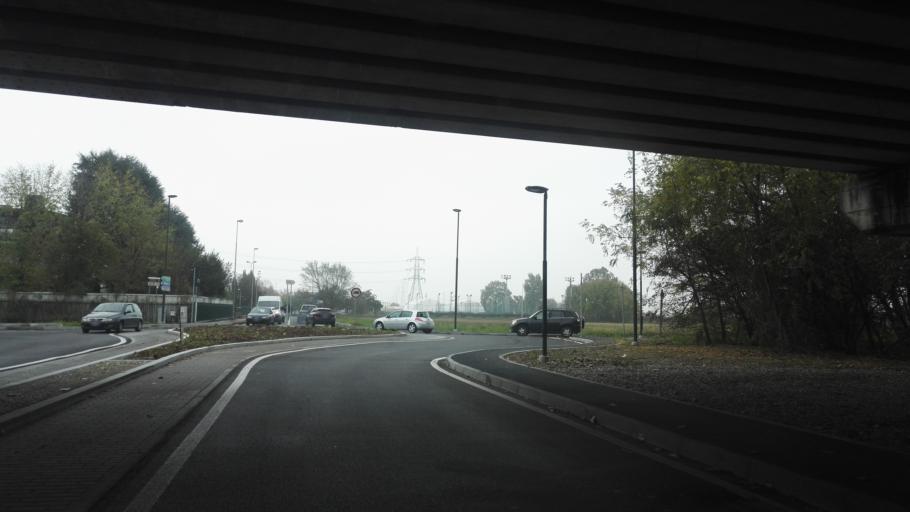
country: IT
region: Lombardy
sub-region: Citta metropolitana di Milano
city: Vighignolo
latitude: 45.4922
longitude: 9.0472
